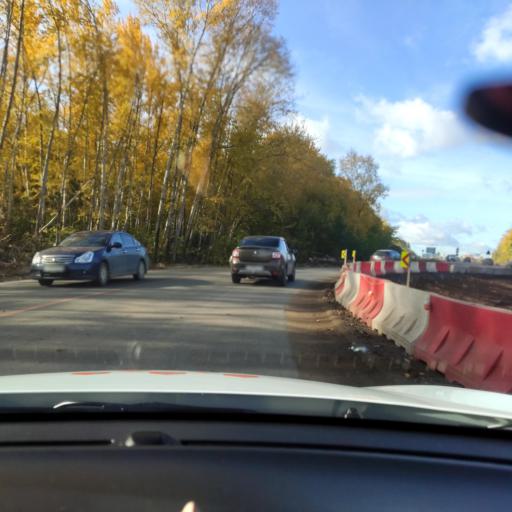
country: RU
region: Tatarstan
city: Vysokaya Gora
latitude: 55.8000
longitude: 49.3552
